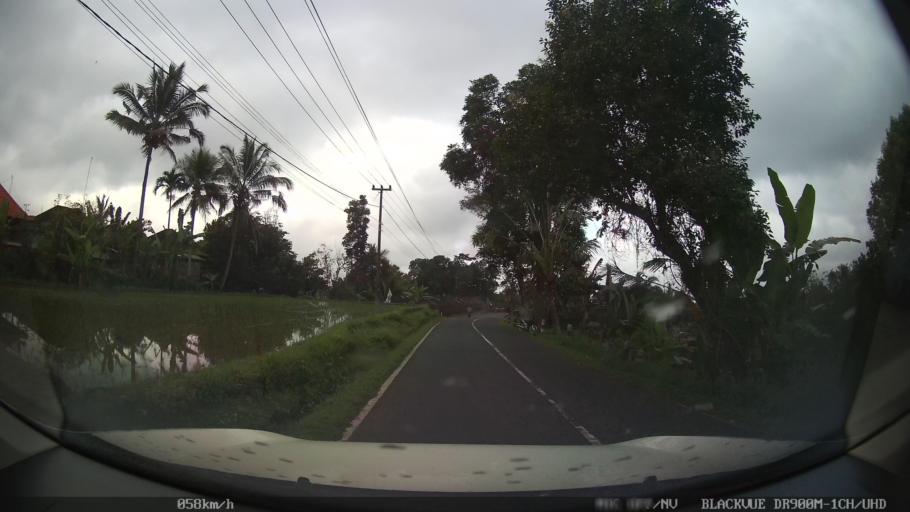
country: ID
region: Bali
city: Empalan
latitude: -8.3922
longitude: 115.1516
